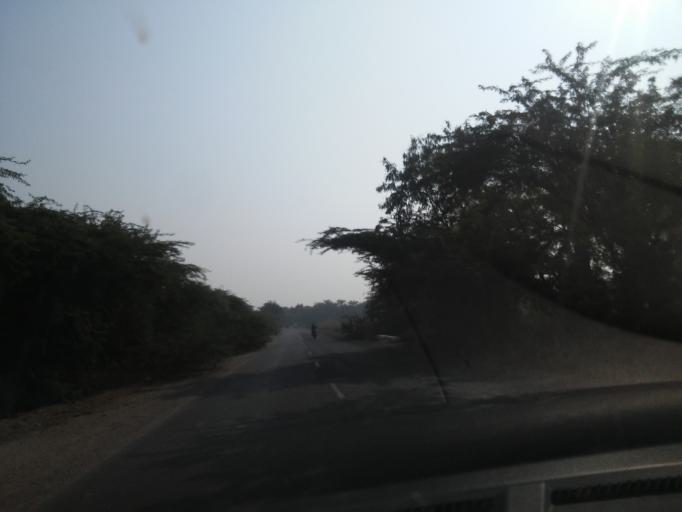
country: IN
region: Gujarat
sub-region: Kachchh
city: Mundra
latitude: 22.8372
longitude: 69.6561
